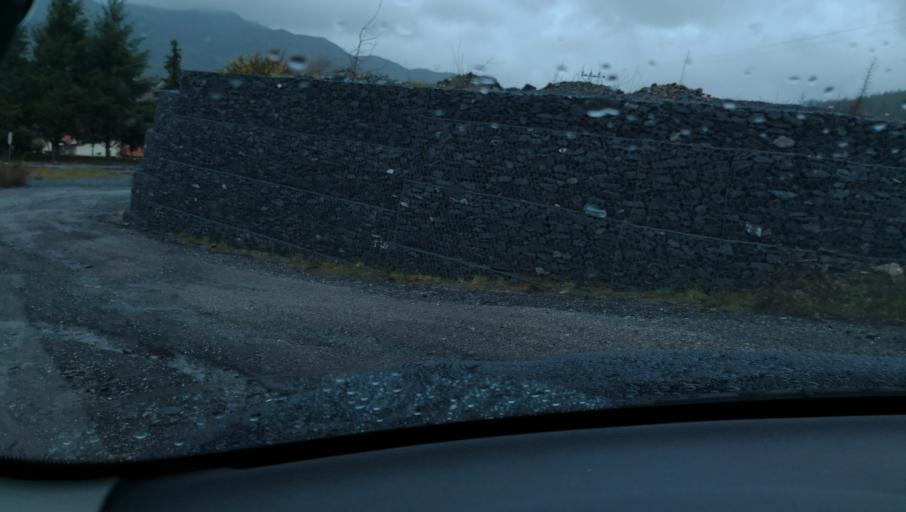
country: PT
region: Vila Real
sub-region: Santa Marta de Penaguiao
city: Santa Marta de Penaguiao
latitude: 41.2812
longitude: -7.8479
